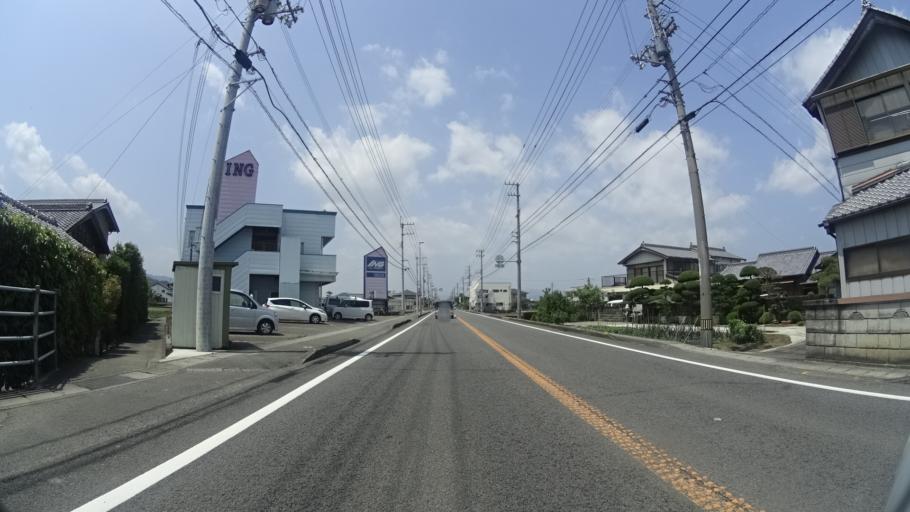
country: JP
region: Tokushima
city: Ishii
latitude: 34.0675
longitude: 134.4163
